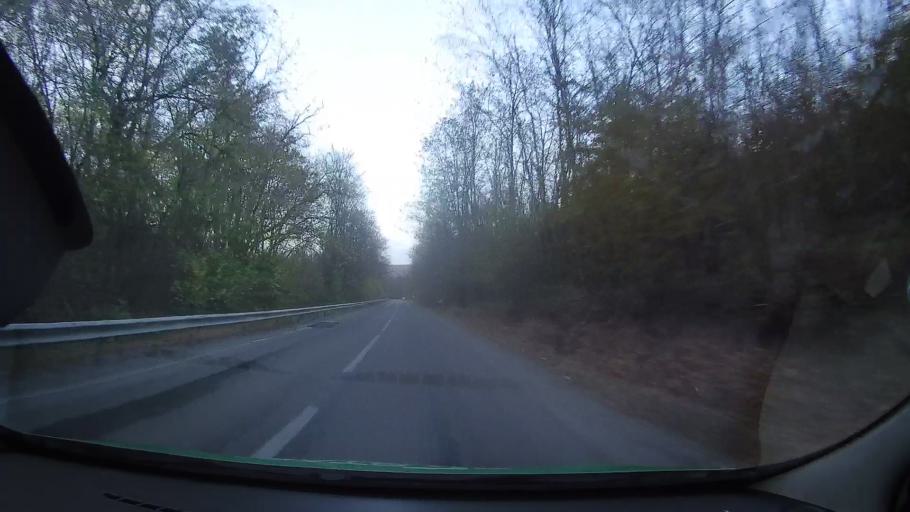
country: RO
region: Constanta
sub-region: Comuna Baneasa
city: Baneasa
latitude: 44.0834
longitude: 27.6674
